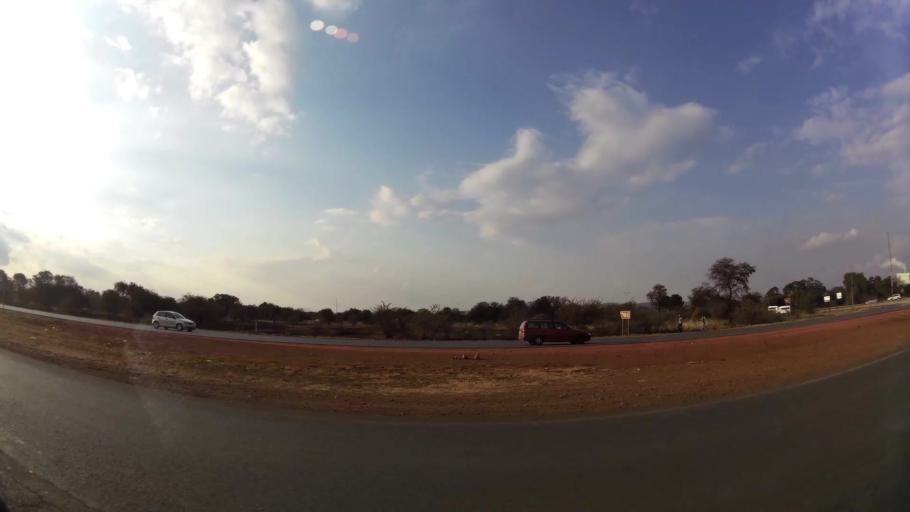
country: ZA
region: Gauteng
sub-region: Sedibeng District Municipality
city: Vanderbijlpark
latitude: -26.6222
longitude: 27.8507
